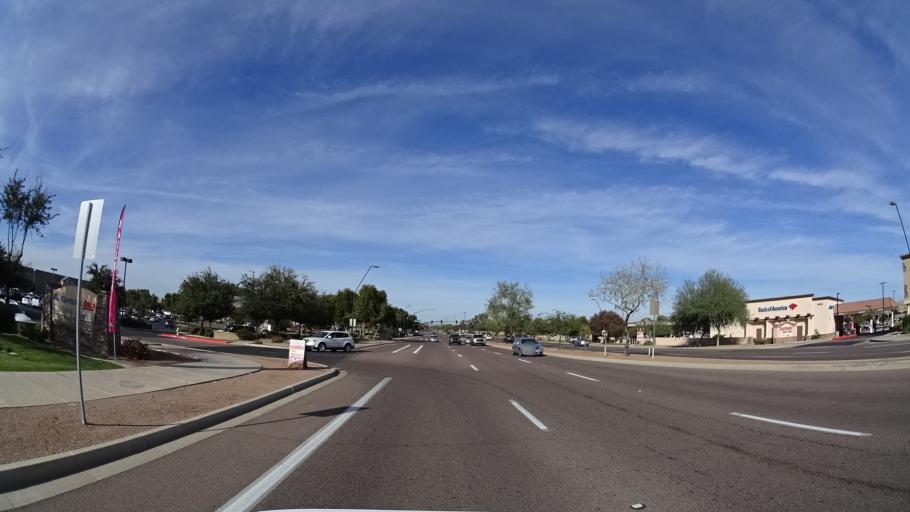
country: US
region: Arizona
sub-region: Maricopa County
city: Queen Creek
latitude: 33.2648
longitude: -111.6862
